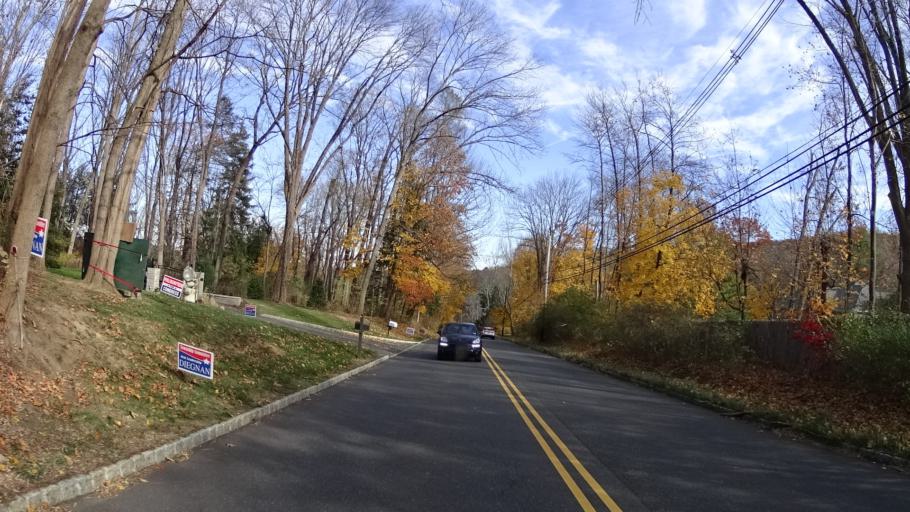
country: US
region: New Jersey
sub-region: Morris County
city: Mendham
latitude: 40.7879
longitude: -74.5579
